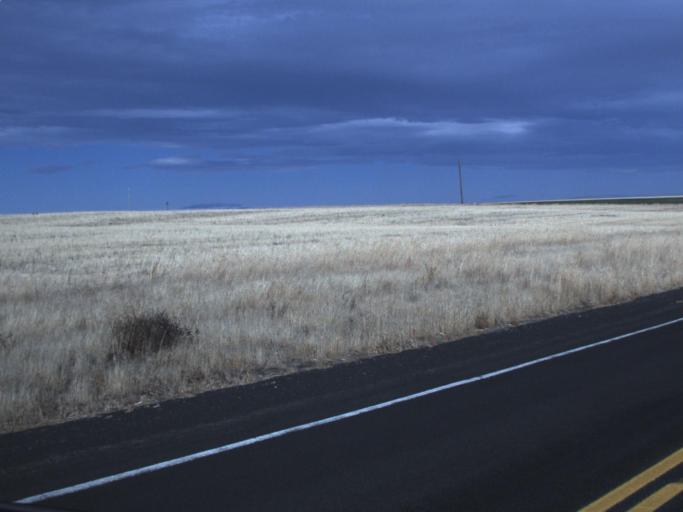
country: US
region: Washington
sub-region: Adams County
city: Ritzville
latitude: 47.2742
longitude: -118.6910
